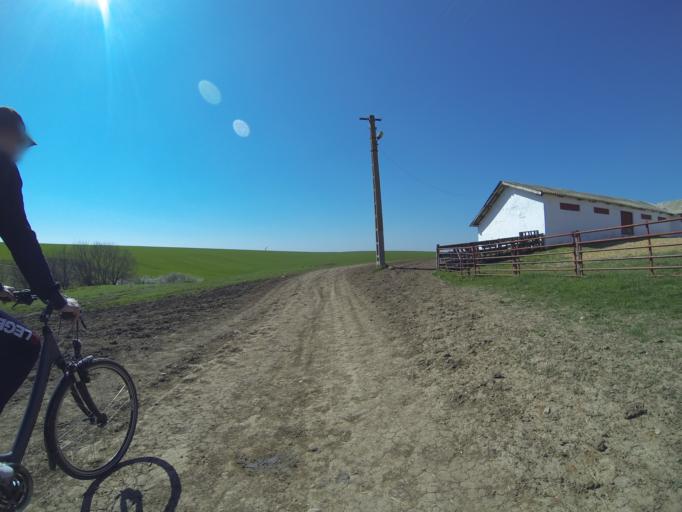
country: RO
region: Dolj
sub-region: Comuna Caloparu
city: Salcuta
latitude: 44.1599
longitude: 23.6656
